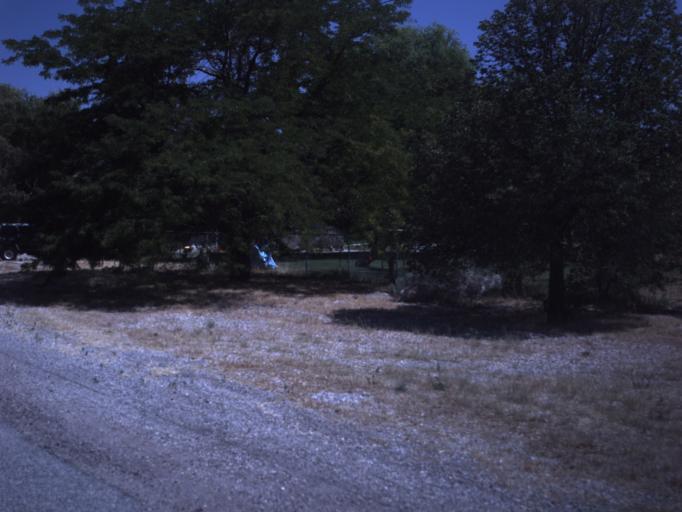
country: US
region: Utah
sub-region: Millard County
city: Delta
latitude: 39.3794
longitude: -112.3360
